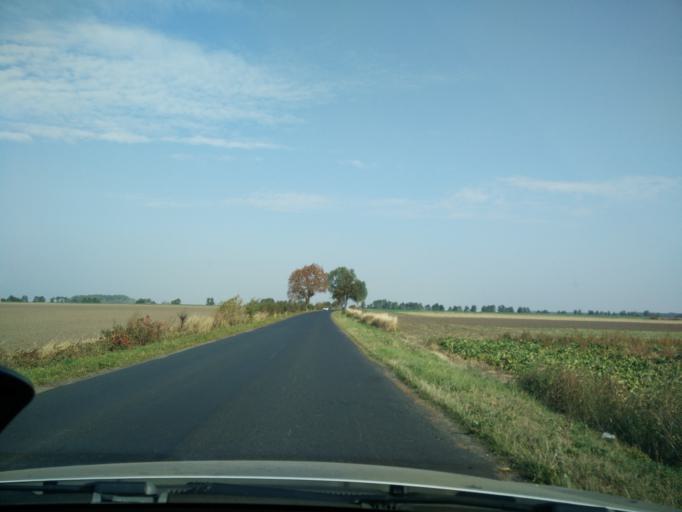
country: PL
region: Greater Poland Voivodeship
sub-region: Powiat sredzki
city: Dominowo
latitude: 52.2716
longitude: 17.3164
